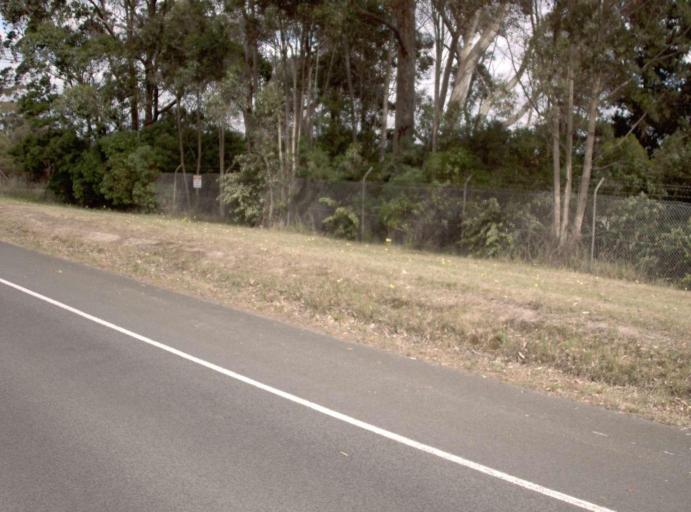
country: AU
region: Victoria
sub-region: Latrobe
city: Morwell
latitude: -38.1869
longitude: 146.4540
